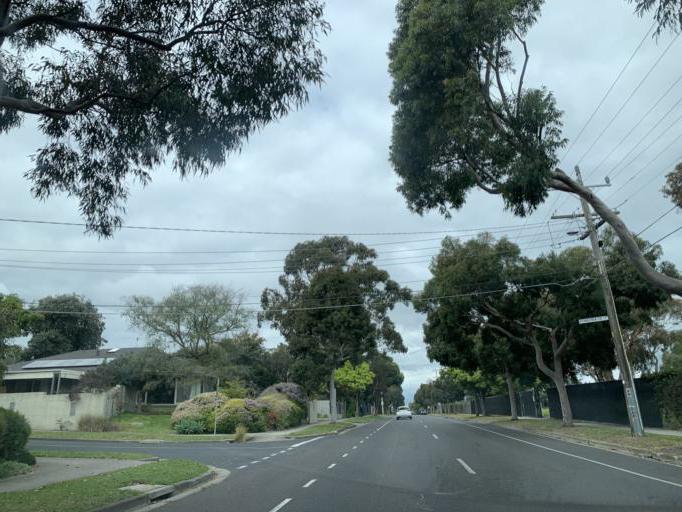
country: AU
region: Victoria
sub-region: Bayside
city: Cheltenham
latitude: -37.9712
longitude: 145.0441
